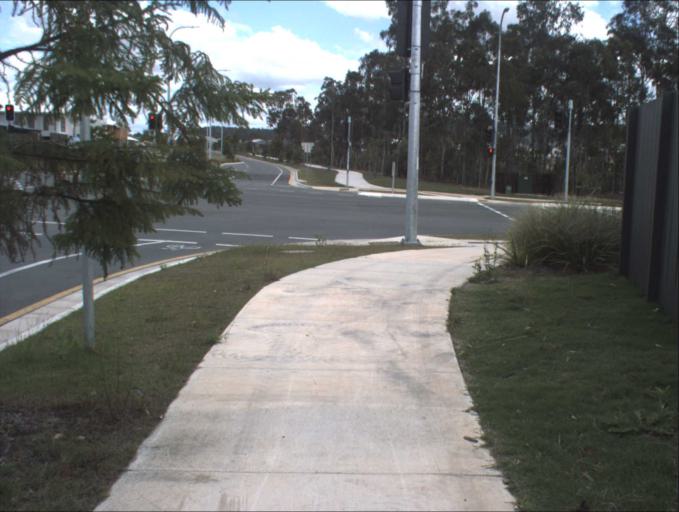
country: AU
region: Queensland
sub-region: Logan
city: Chambers Flat
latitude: -27.8046
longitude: 153.1117
